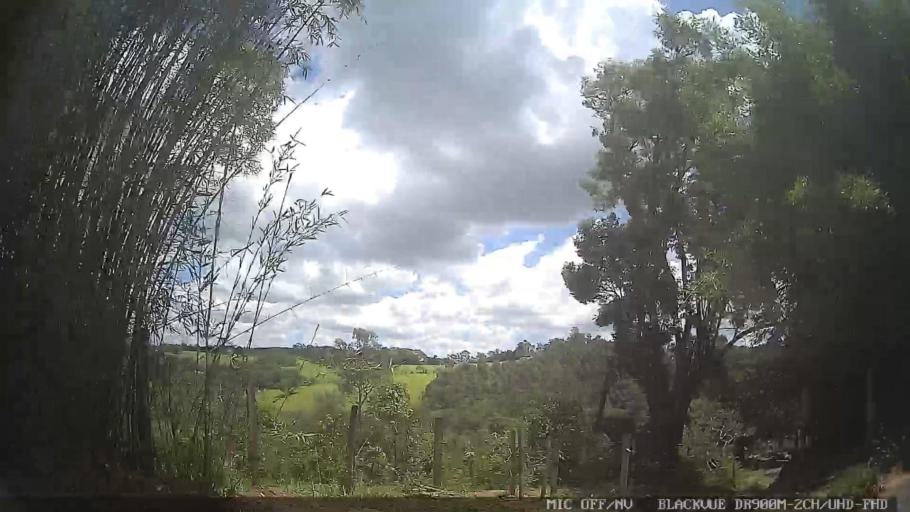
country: BR
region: Sao Paulo
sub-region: Piracaia
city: Piracaia
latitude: -23.0026
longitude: -46.4497
